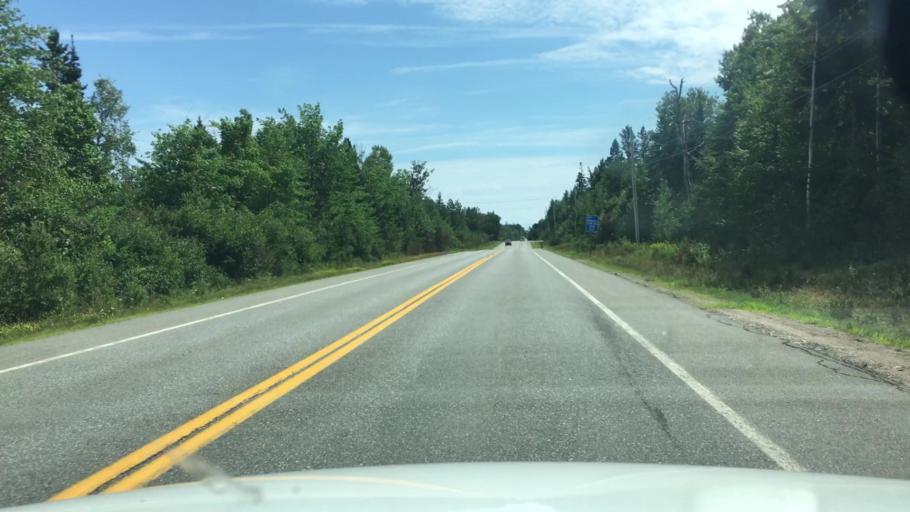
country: CA
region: New Brunswick
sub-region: Charlotte County
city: Saint Andrews
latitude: 45.0027
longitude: -67.0906
